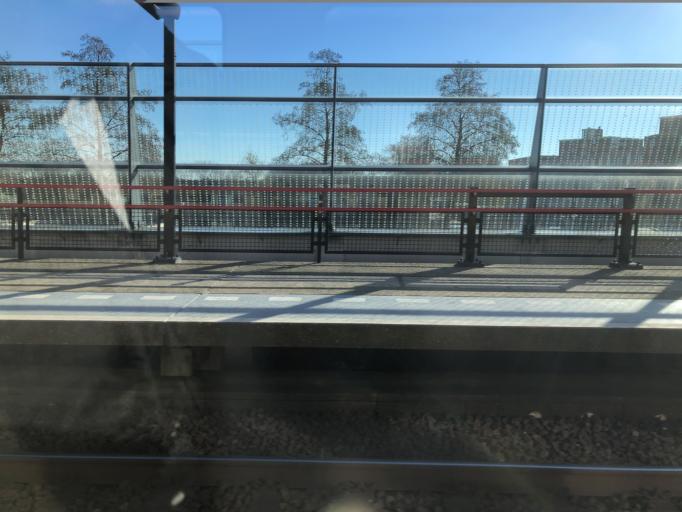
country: NL
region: Flevoland
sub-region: Gemeente Almere
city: Almere Stad
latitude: 52.3684
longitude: 5.1913
